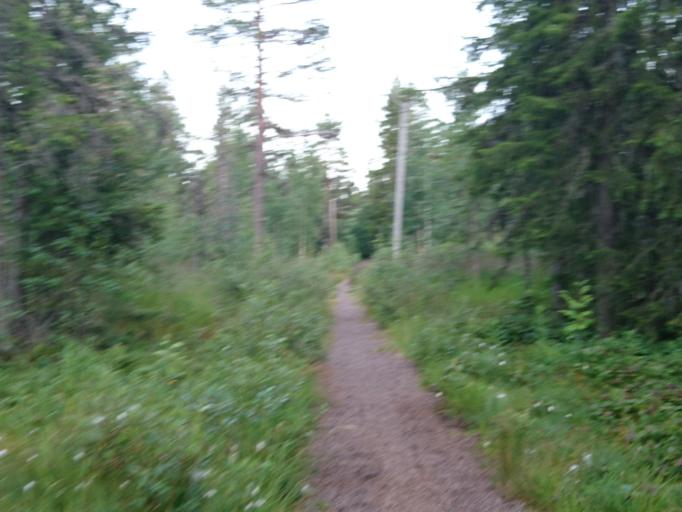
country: SE
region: Dalarna
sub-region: Malung-Saelens kommun
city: Malung
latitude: 61.1711
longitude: 13.1707
